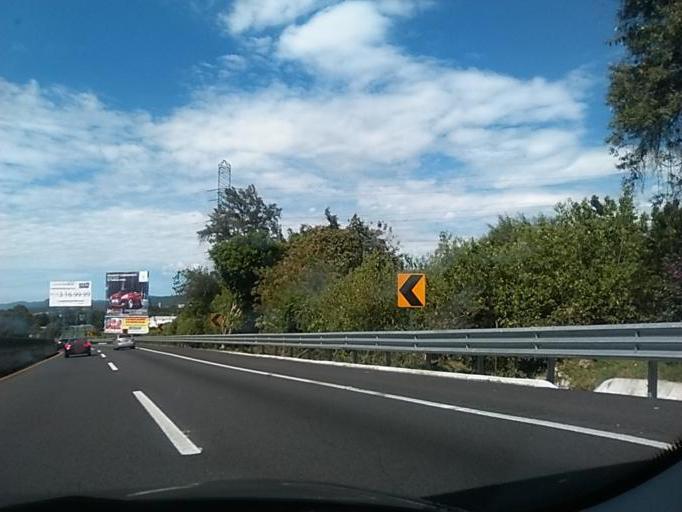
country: MX
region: Morelos
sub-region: Cuernavaca
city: Fraccionamiento Lomas de Ahuatlan
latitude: 18.9816
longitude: -99.2289
